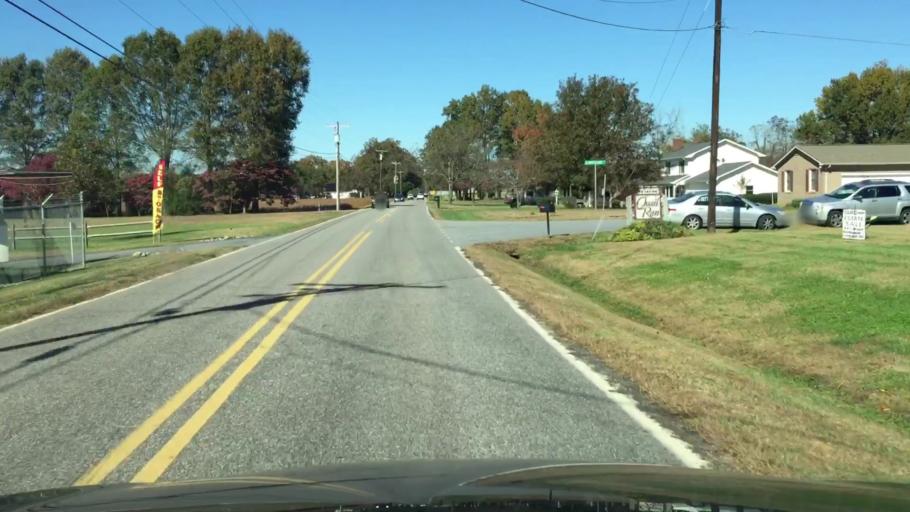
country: US
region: North Carolina
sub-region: Iredell County
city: Mooresville
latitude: 35.5618
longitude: -80.7749
